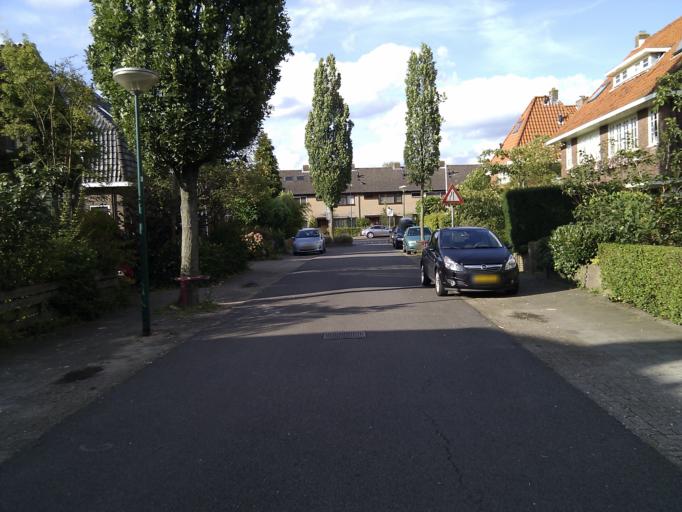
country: NL
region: Utrecht
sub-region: Gemeente De Bilt
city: De Bilt
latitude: 52.1061
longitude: 5.1725
